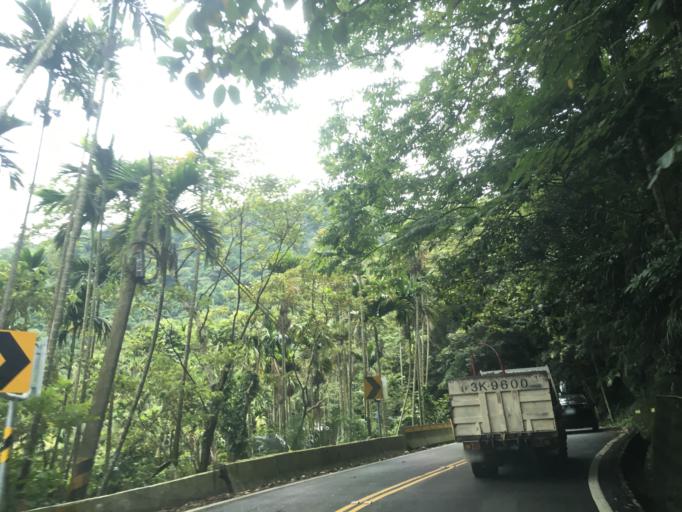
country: TW
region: Taiwan
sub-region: Yunlin
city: Douliu
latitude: 23.5604
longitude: 120.5873
